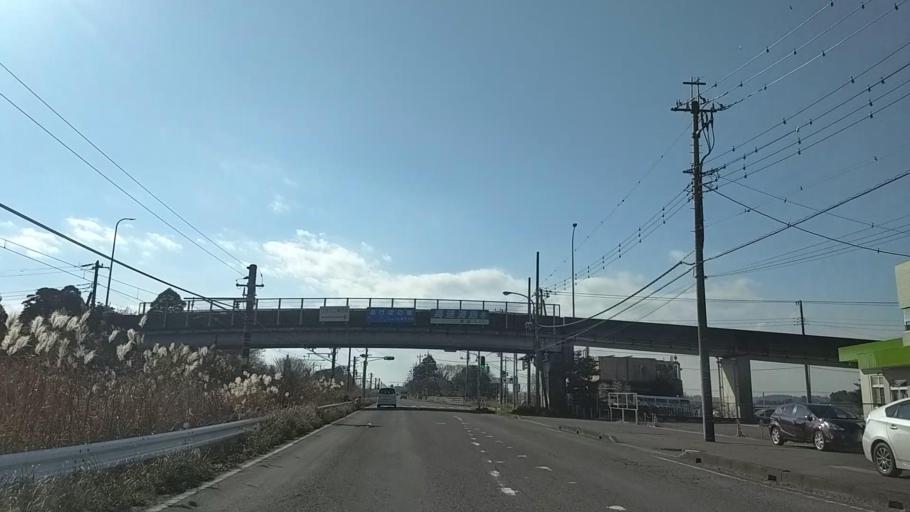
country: JP
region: Chiba
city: Yokaichiba
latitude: 35.6763
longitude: 140.5106
